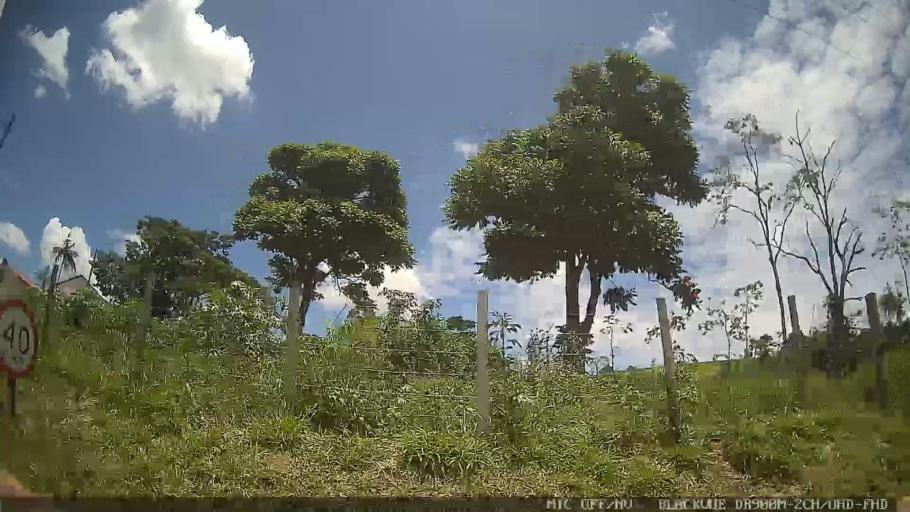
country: BR
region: Sao Paulo
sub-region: Santa Branca
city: Santa Branca
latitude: -23.5258
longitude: -45.8592
